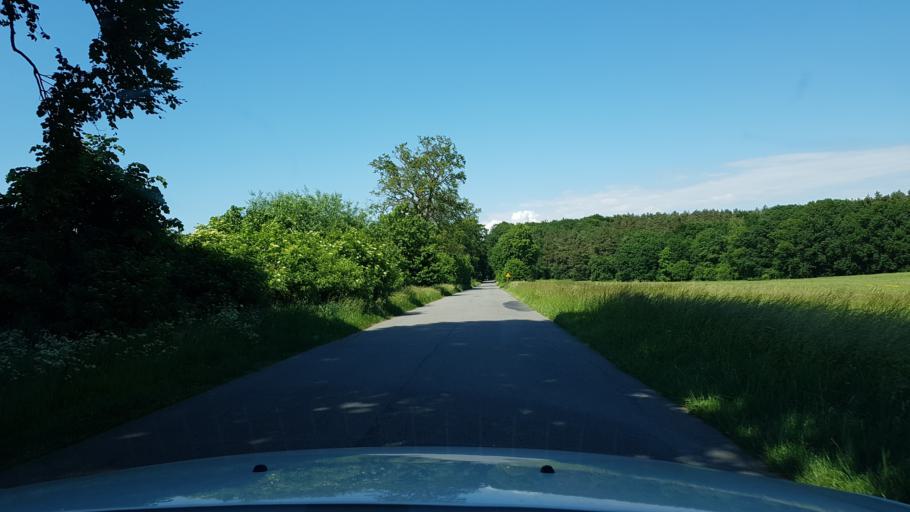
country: PL
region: West Pomeranian Voivodeship
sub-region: Powiat gryfinski
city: Banie
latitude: 53.0504
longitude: 14.6264
